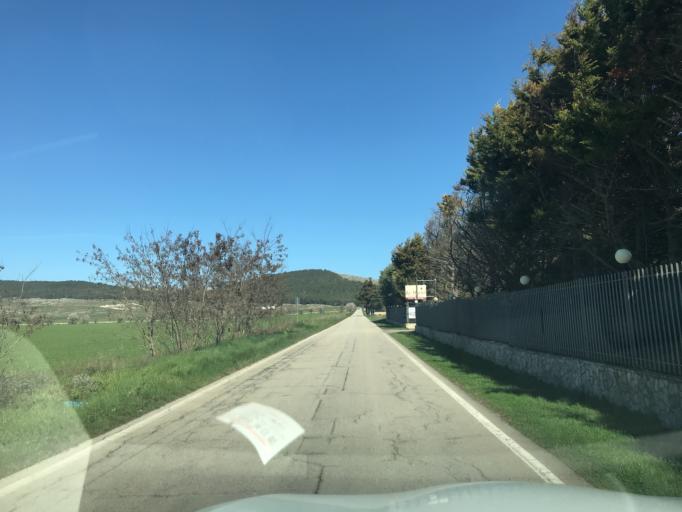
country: IT
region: Apulia
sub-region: Provincia di Bari
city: Gravina in Puglia
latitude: 40.8630
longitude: 16.4380
